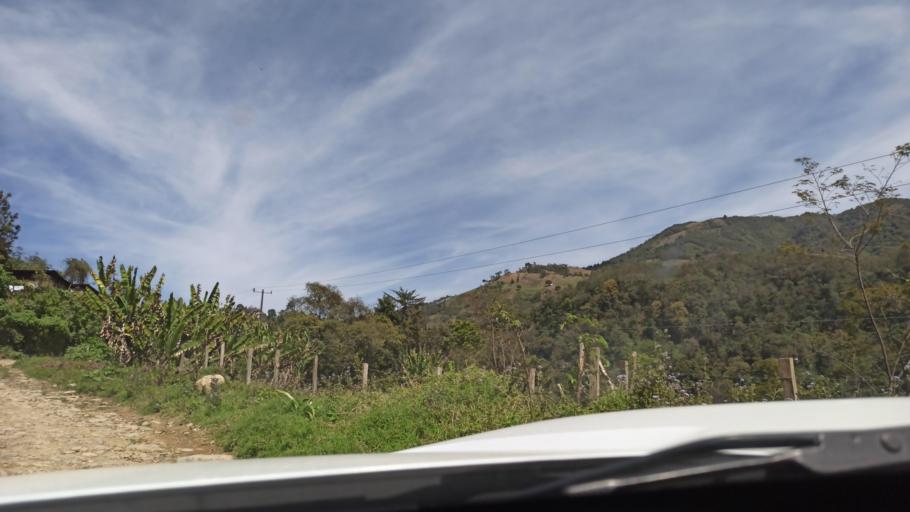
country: MX
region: Veracruz
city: Xocotla
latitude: 18.9877
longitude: -97.0992
